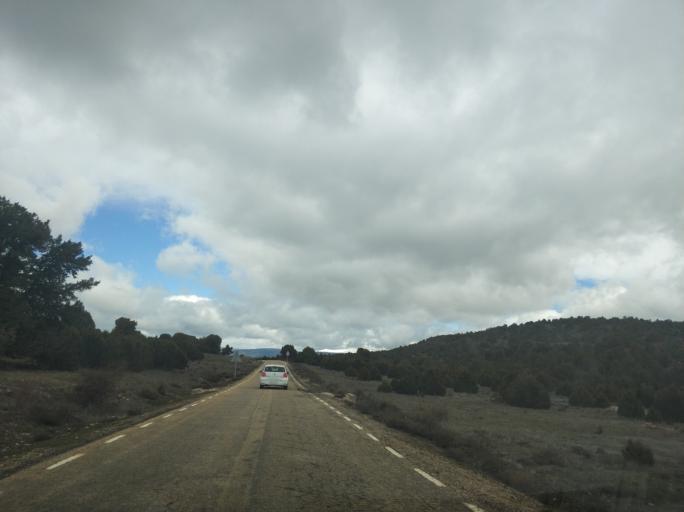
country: ES
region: Castille and Leon
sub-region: Provincia de Soria
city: Abejar
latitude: 41.7877
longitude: -2.7690
